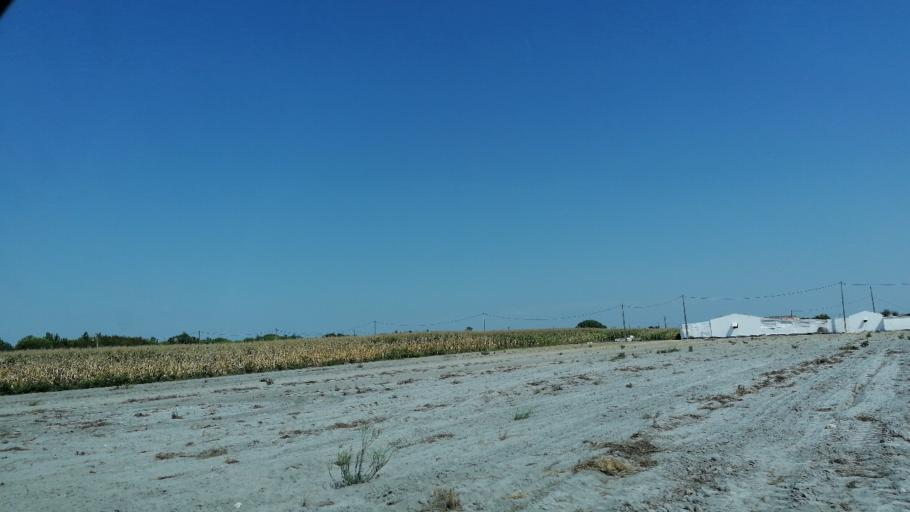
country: PT
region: Santarem
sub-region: Benavente
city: Poceirao
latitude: 38.7207
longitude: -8.7098
